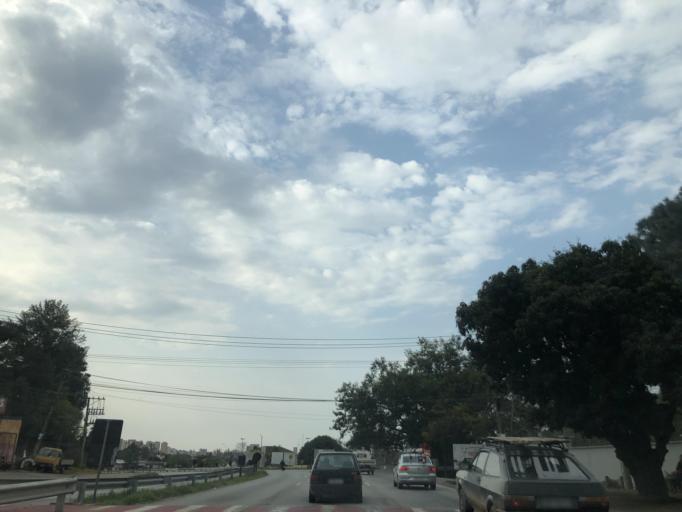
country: BR
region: Sao Paulo
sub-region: Votorantim
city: Votorantim
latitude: -23.5464
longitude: -47.4831
